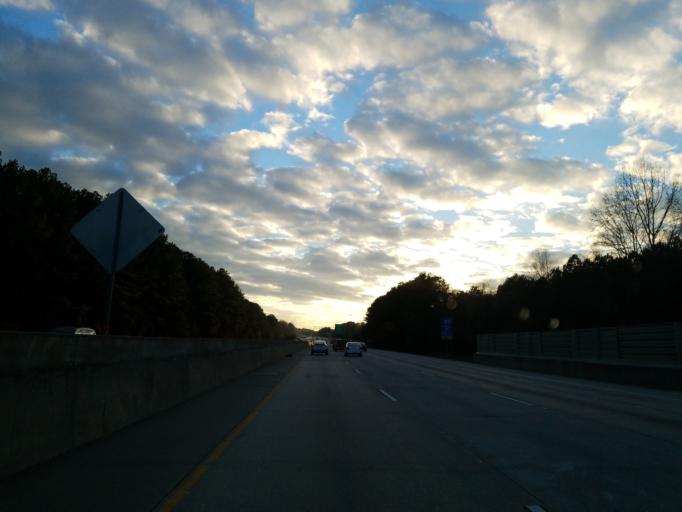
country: US
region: Georgia
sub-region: Fulton County
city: Alpharetta
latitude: 34.0972
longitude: -84.2517
